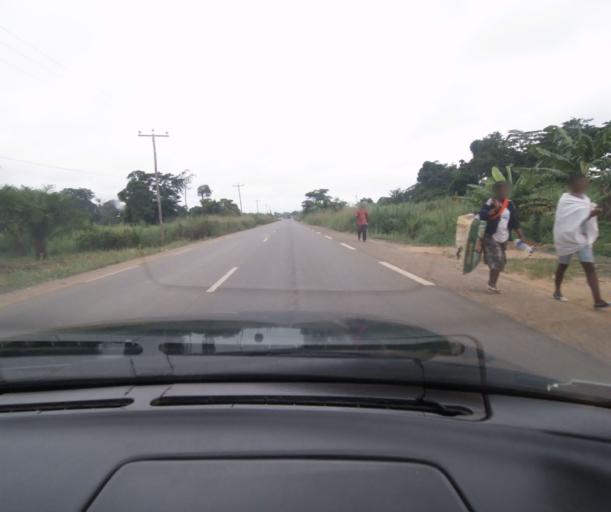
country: CM
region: Centre
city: Saa
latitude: 4.3575
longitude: 11.2766
